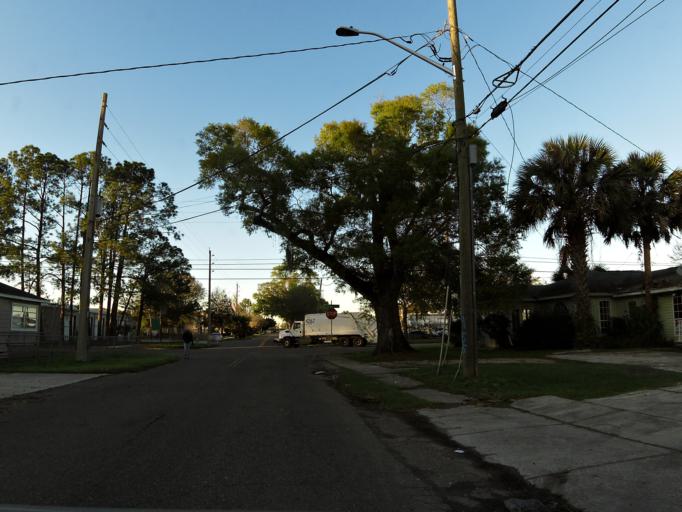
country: US
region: Florida
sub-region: Duval County
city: Jacksonville
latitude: 30.3363
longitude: -81.7098
